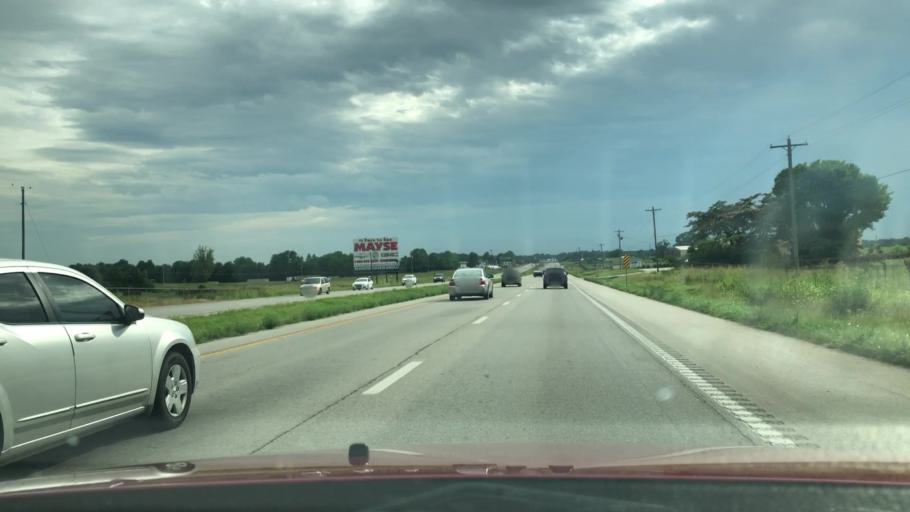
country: US
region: Missouri
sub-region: Greene County
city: Battlefield
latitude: 37.1575
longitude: -93.4070
